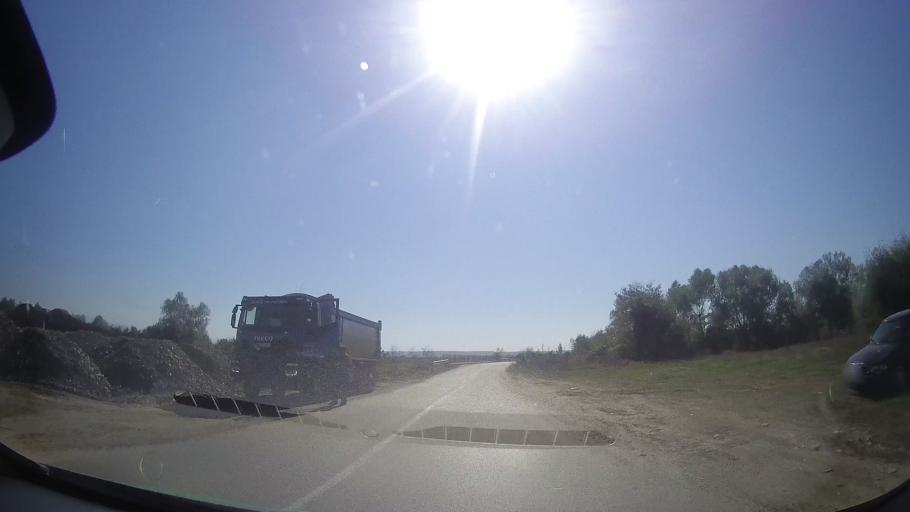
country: RO
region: Timis
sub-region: Comuna Bethausen
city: Bethausen
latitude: 45.8303
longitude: 21.9596
